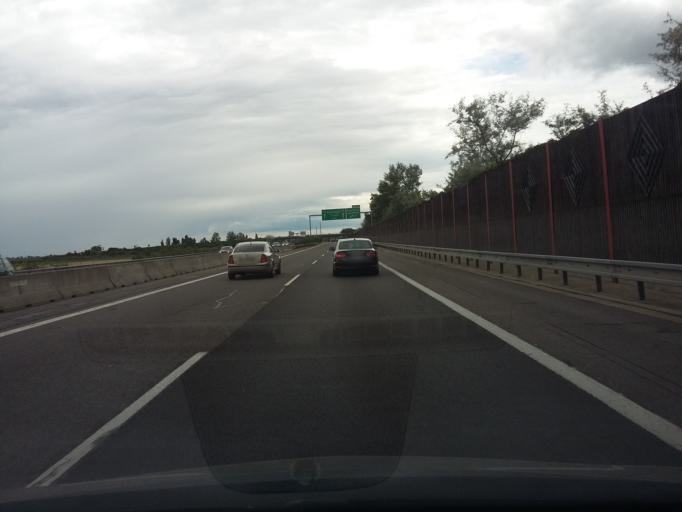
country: SK
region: Trenciansky
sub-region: Okres Nove Mesto nad Vahom
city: Nove Mesto nad Vahom
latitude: 48.7665
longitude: 17.8719
